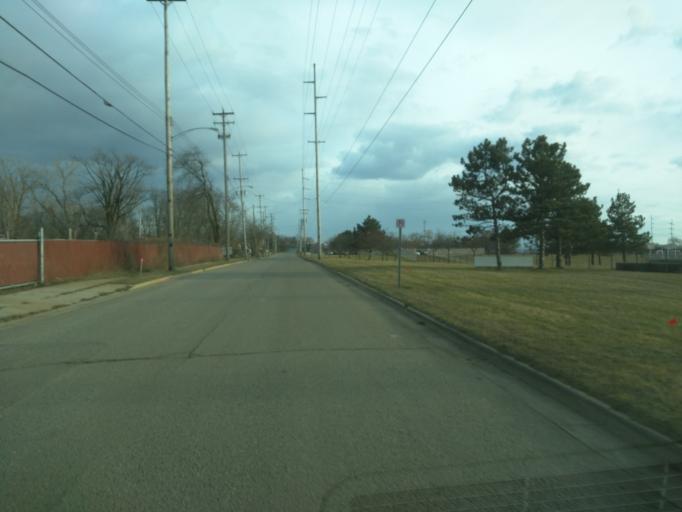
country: US
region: Michigan
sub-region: Ingham County
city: Edgemont Park
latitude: 42.7519
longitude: -84.5794
